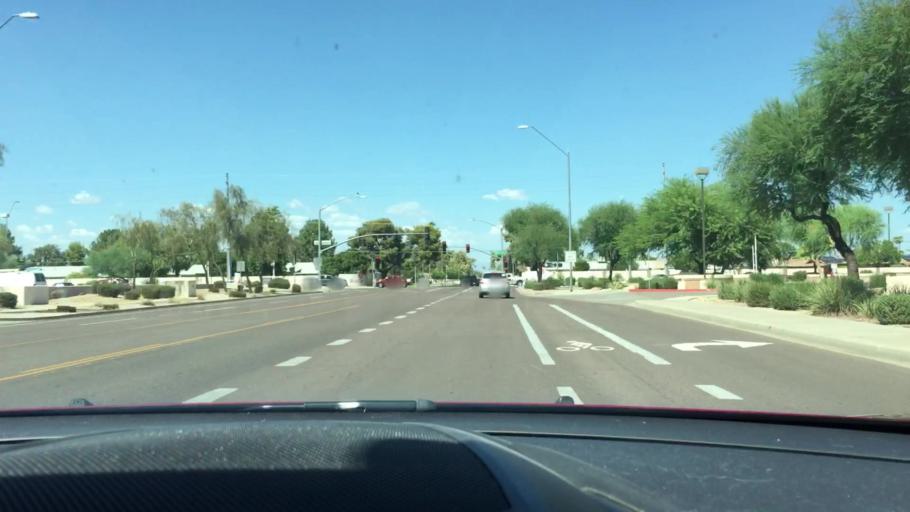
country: US
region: Arizona
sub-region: Maricopa County
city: Youngtown
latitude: 33.5647
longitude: -112.2902
